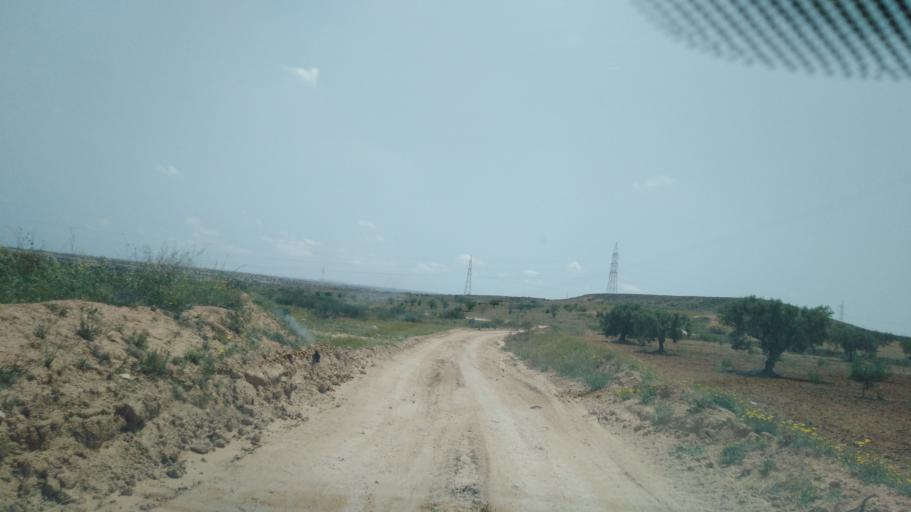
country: TN
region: Safaqis
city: Sfax
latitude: 34.7661
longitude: 10.5811
